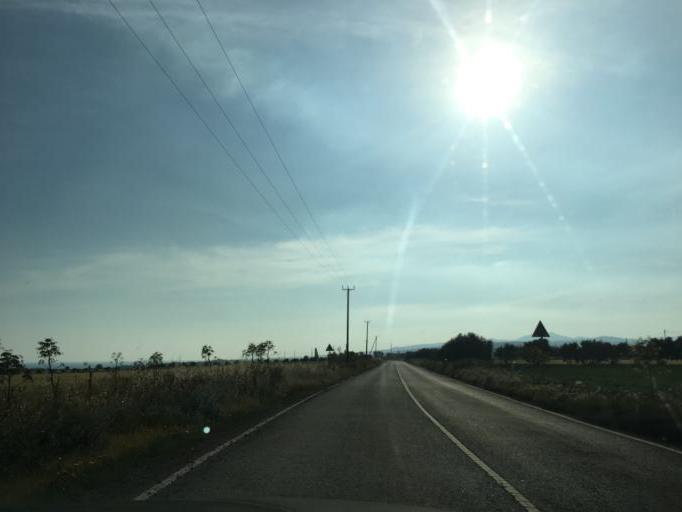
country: CY
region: Larnaka
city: Kofinou
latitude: 34.7836
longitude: 33.4781
